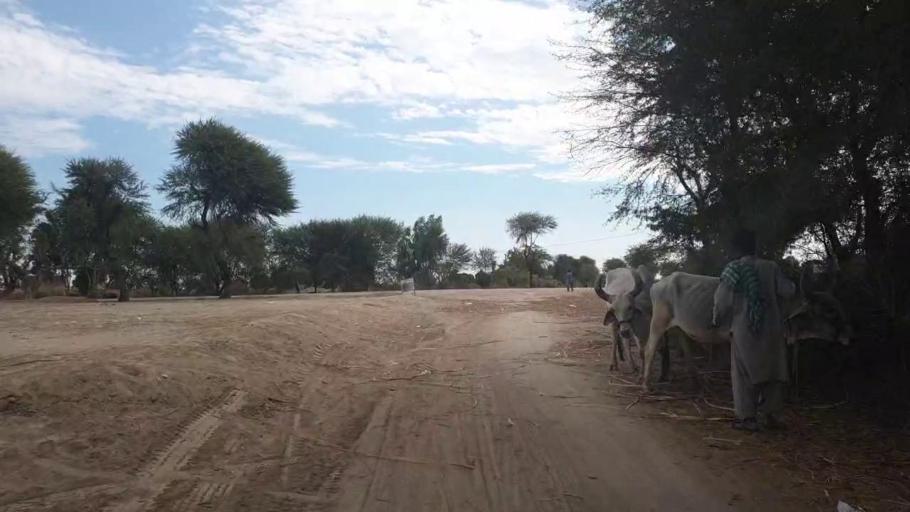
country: PK
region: Sindh
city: Jhol
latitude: 25.9848
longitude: 68.9014
